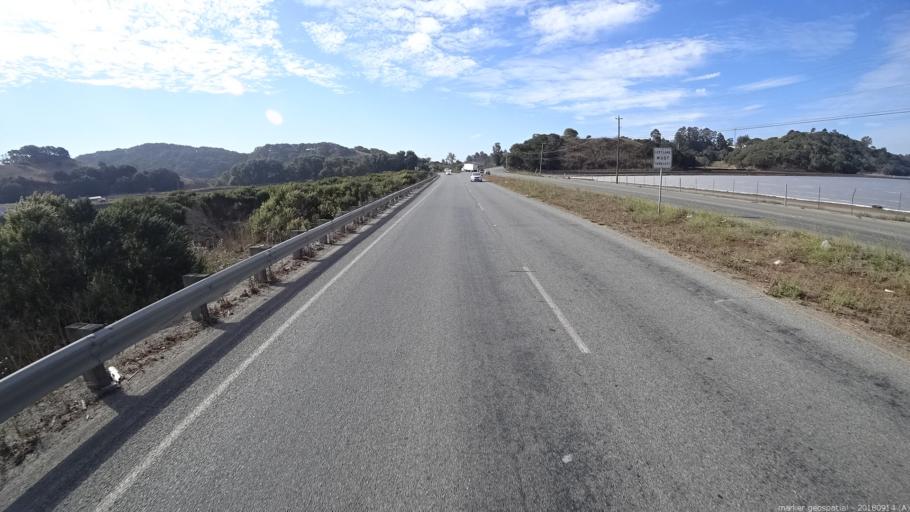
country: US
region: California
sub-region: Monterey County
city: Pajaro
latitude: 36.8838
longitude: -121.7468
